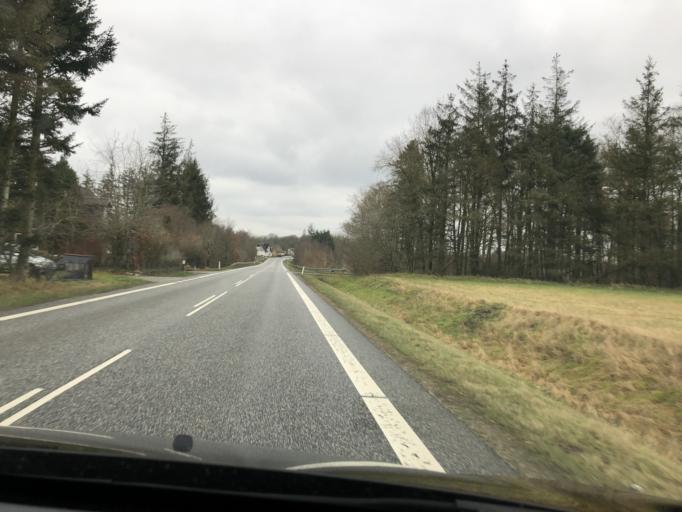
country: DK
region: South Denmark
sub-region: Billund Kommune
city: Grindsted
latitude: 55.8557
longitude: 8.7907
